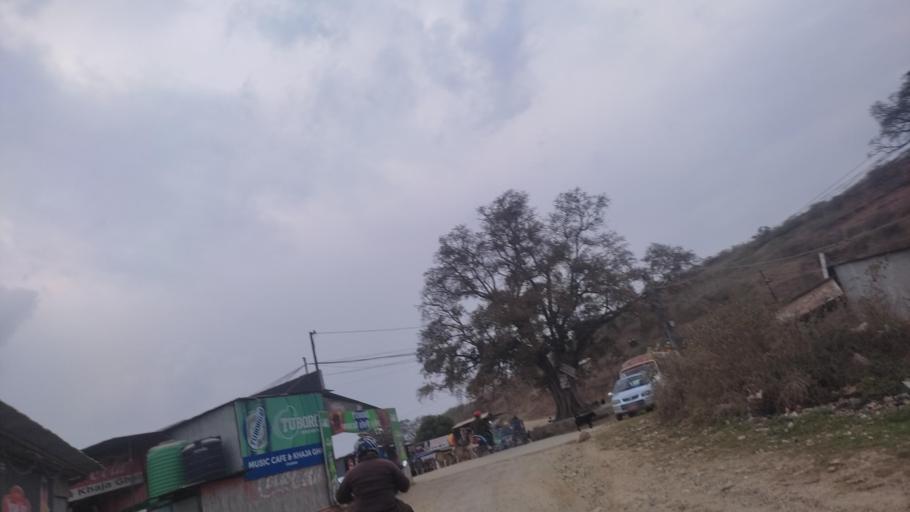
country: NP
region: Central Region
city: Kirtipur
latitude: 27.6626
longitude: 85.2884
